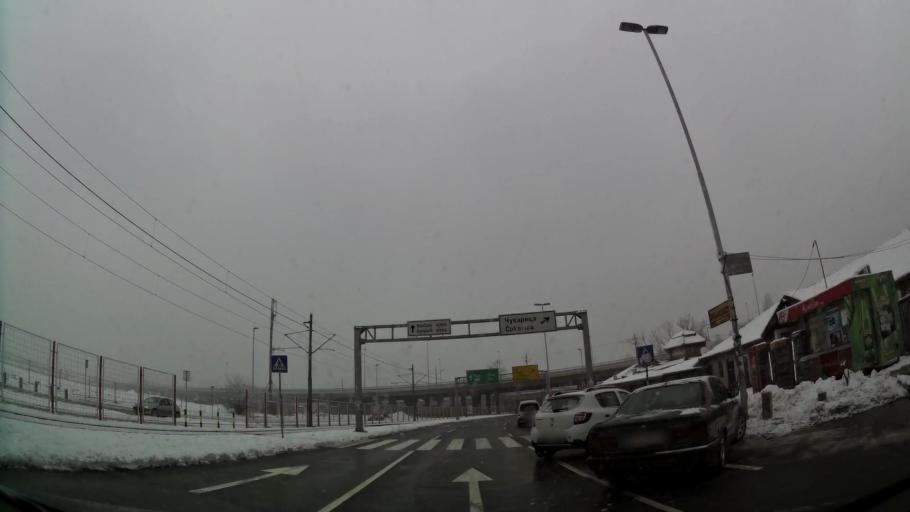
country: RS
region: Central Serbia
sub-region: Belgrade
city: Novi Beograd
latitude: 44.8048
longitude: 20.4174
